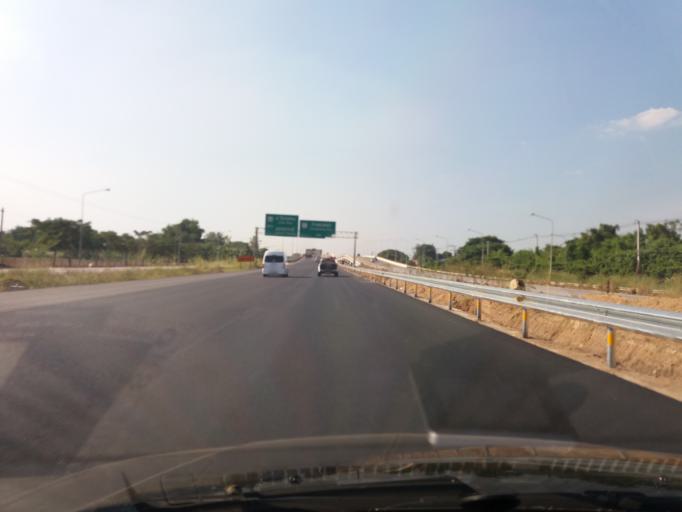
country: TH
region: Nakhon Sawan
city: Nakhon Sawan
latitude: 15.6305
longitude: 100.1044
